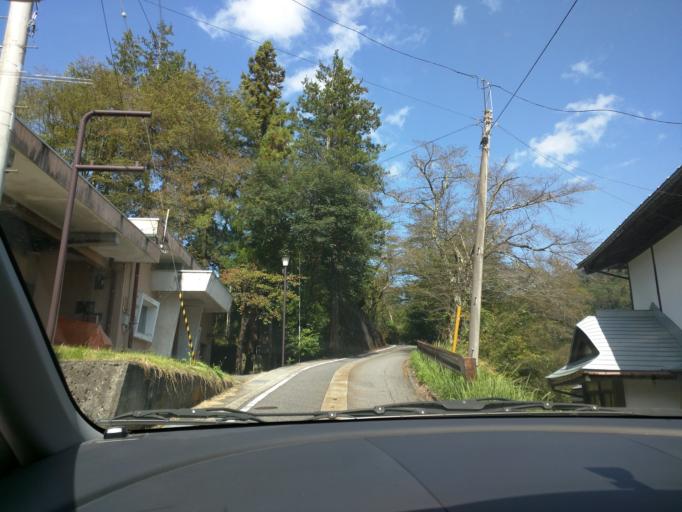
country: JP
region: Fukushima
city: Kitakata
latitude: 37.5293
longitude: 139.7247
